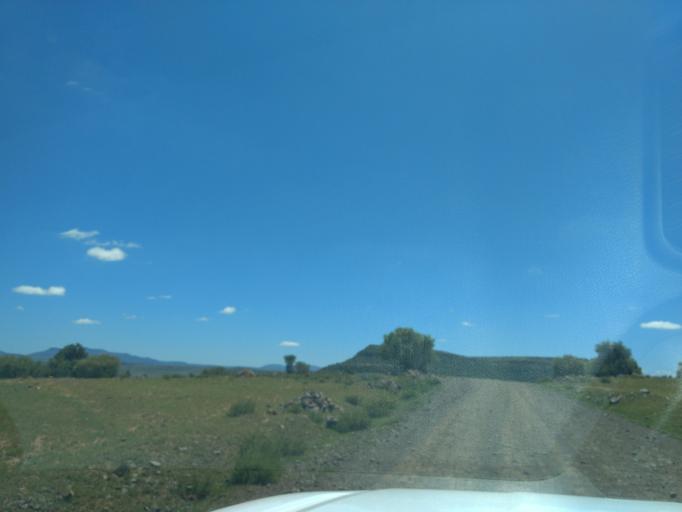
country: LS
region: Maseru
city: Maseru
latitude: -29.4555
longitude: 27.3680
